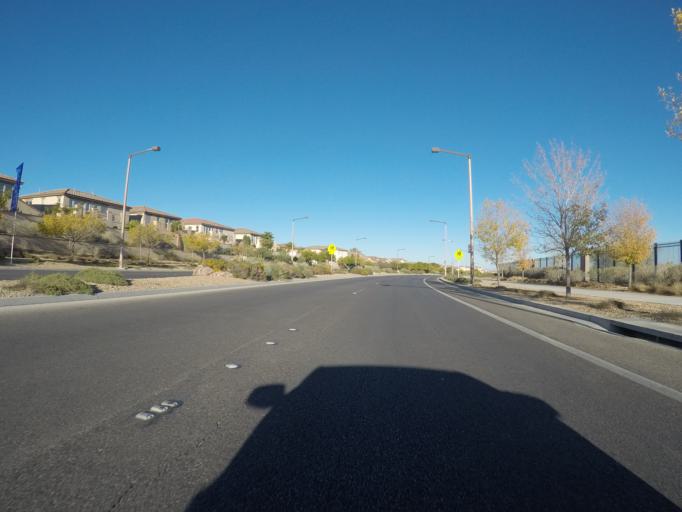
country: US
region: Nevada
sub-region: Clark County
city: Summerlin South
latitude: 36.1583
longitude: -115.3595
